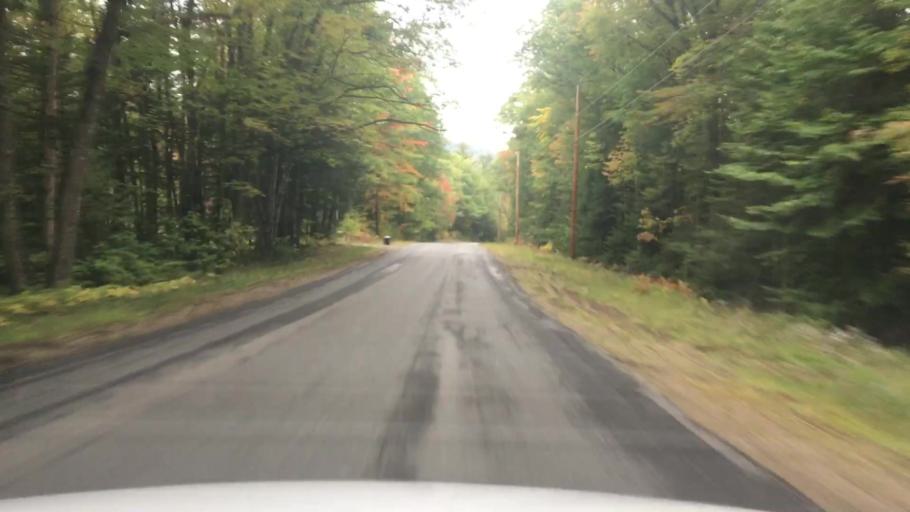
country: US
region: Maine
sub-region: Oxford County
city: Bethel
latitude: 44.4410
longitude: -70.7945
